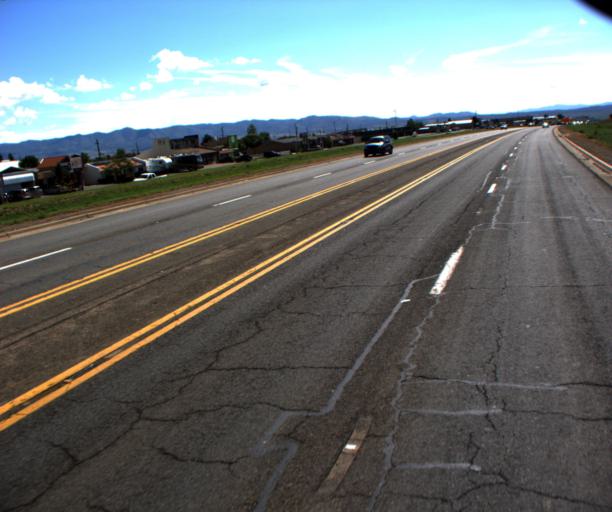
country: US
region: Arizona
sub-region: Yavapai County
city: Prescott Valley
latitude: 34.5851
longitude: -112.3158
